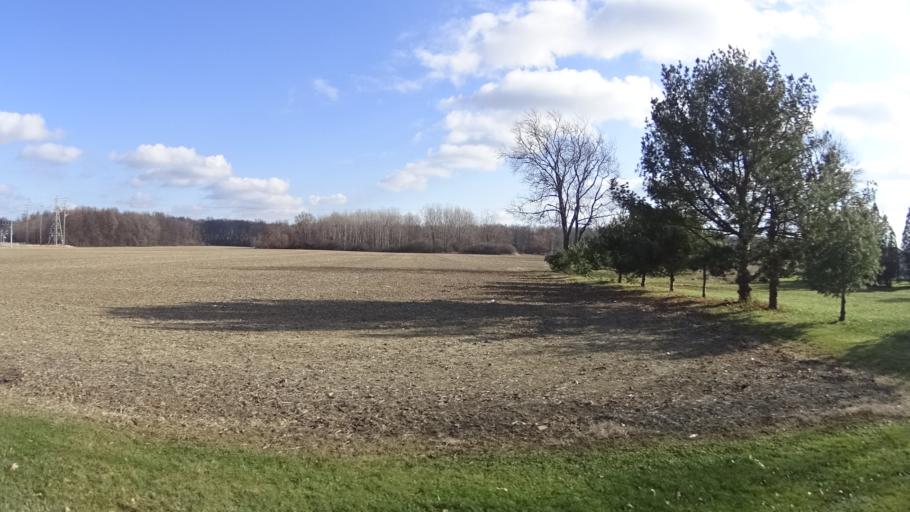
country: US
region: Ohio
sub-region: Lorain County
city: Camden
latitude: 41.2589
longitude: -82.2745
